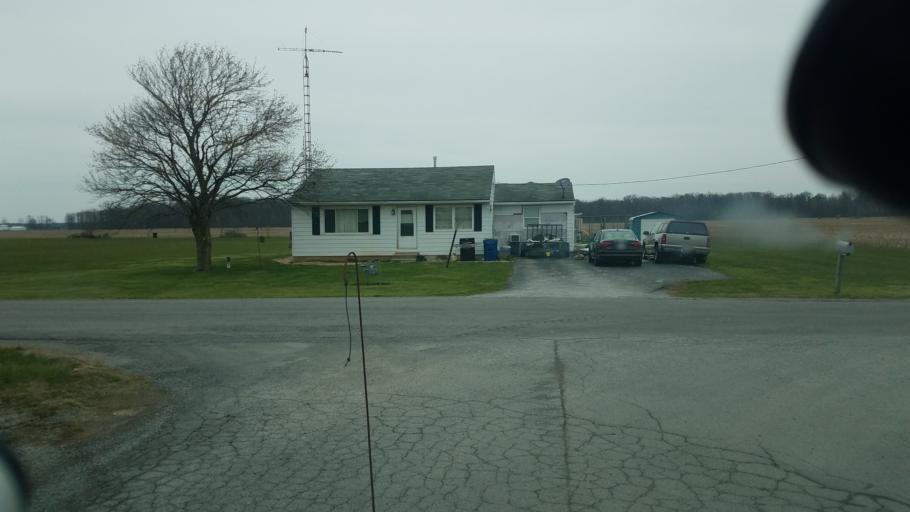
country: US
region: Ohio
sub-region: Hardin County
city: Forest
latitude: 40.8907
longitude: -83.5271
